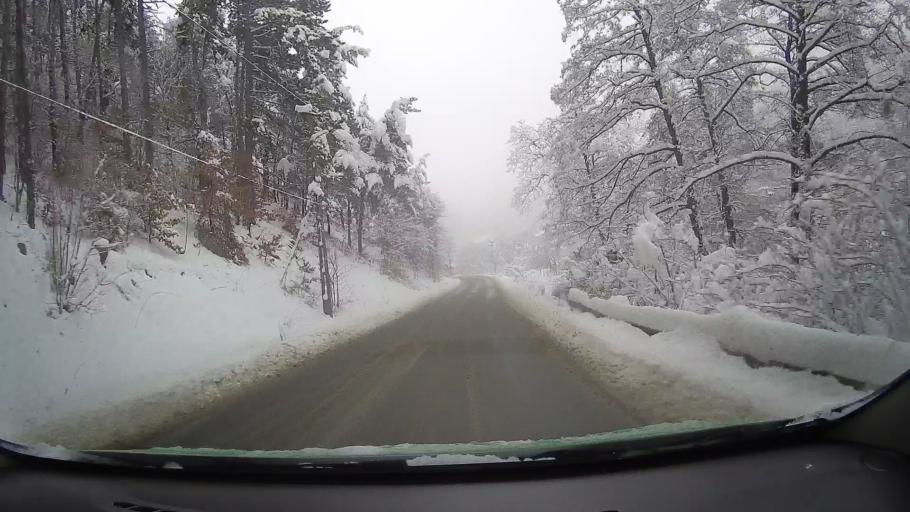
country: RO
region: Sibiu
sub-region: Comuna Tilisca
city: Tilisca
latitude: 45.7995
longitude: 23.8558
